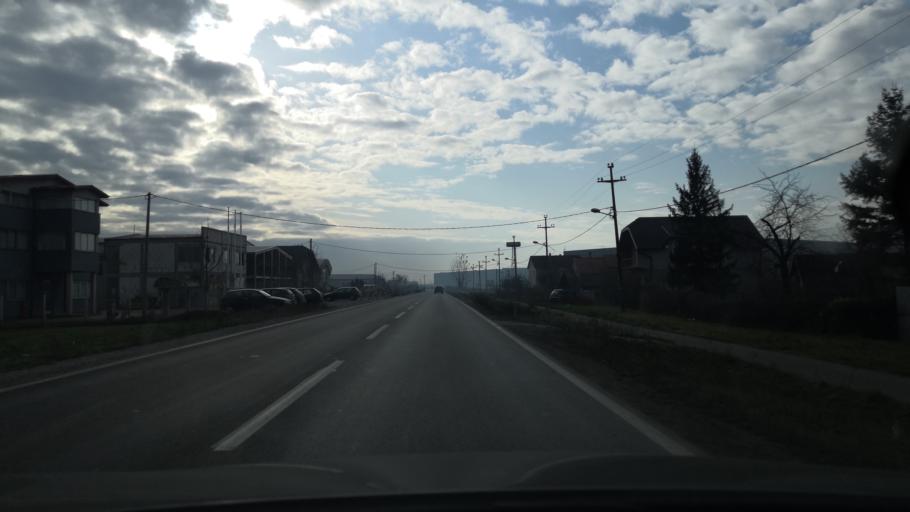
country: RS
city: Ugrinovci
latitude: 44.8572
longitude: 20.2051
